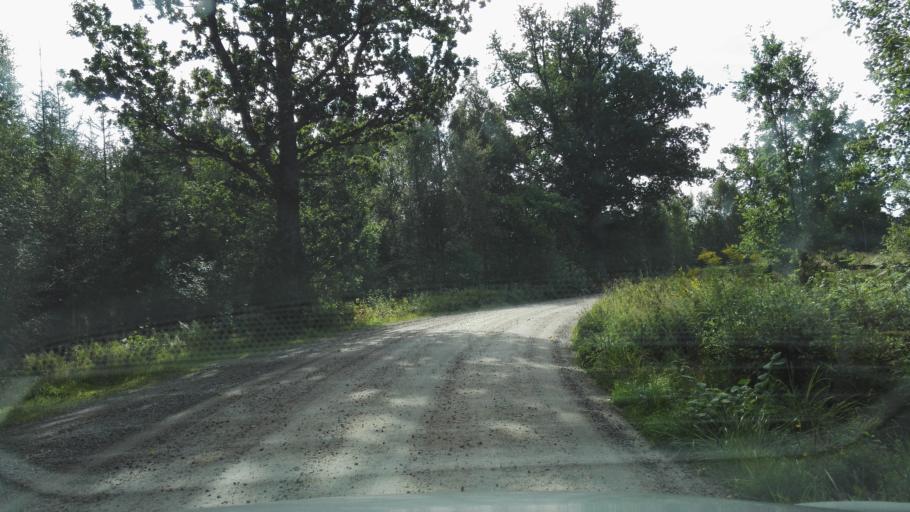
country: SE
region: Kronoberg
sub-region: Vaxjo Kommun
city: Gemla
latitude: 56.8870
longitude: 14.7025
